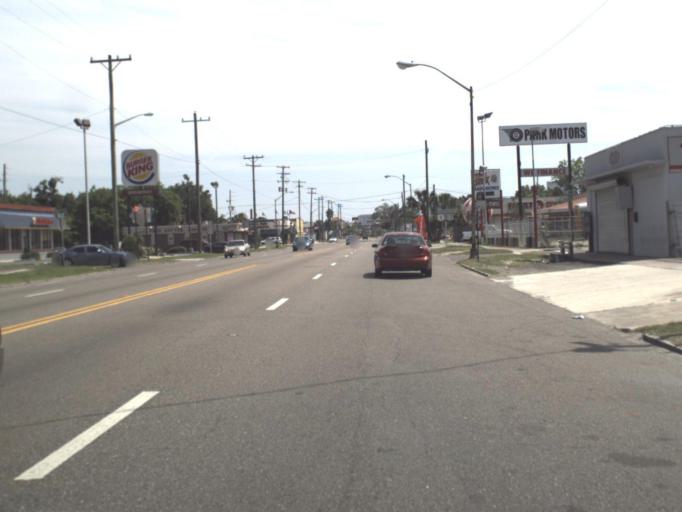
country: US
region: Florida
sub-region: Duval County
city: Jacksonville
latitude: 30.3555
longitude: -81.6540
